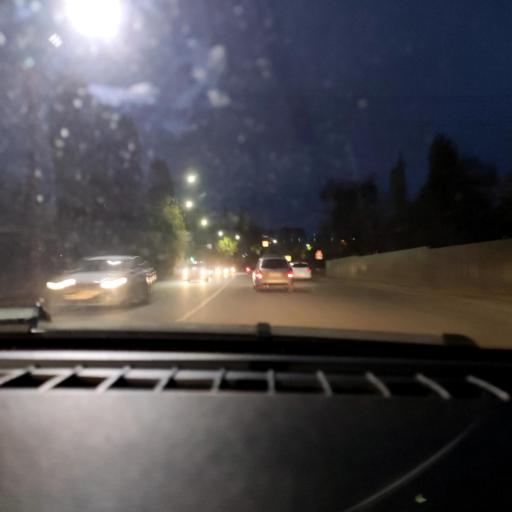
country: RU
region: Voronezj
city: Maslovka
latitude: 51.6297
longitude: 39.2620
